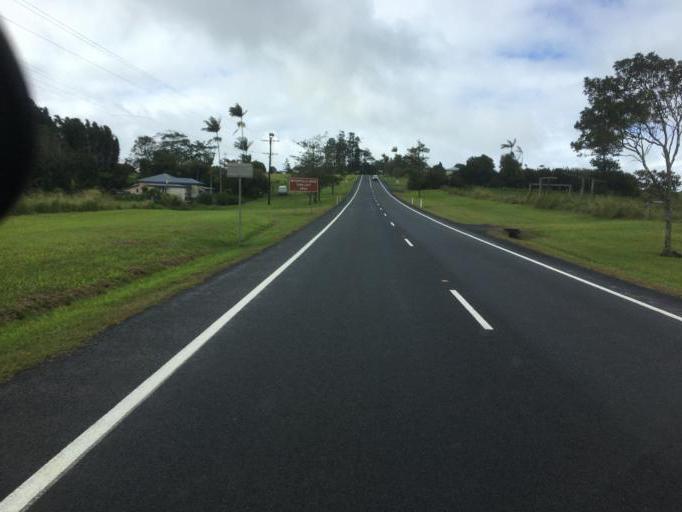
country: AU
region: Queensland
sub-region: Tablelands
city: Ravenshoe
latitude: -17.5087
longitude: 145.6183
